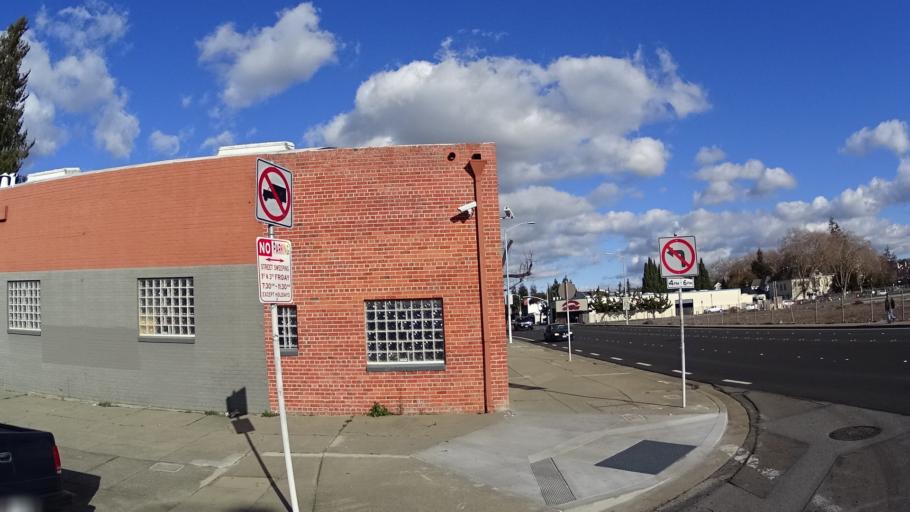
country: US
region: California
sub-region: Alameda County
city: Hayward
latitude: 37.6714
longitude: -122.0891
